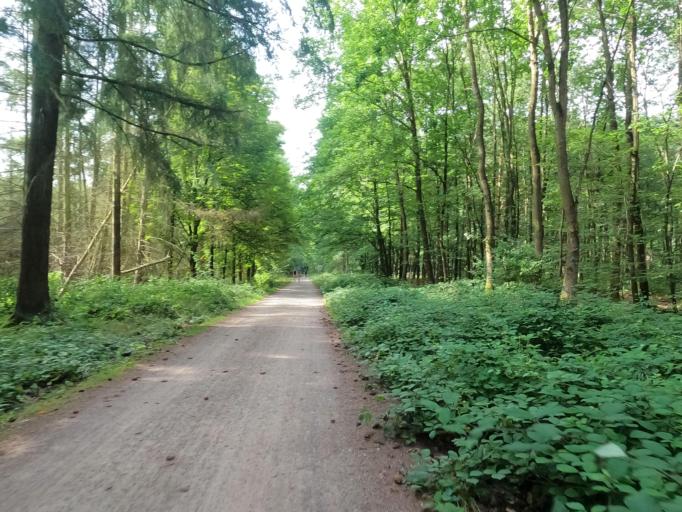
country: DE
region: Hesse
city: Langen
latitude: 50.0220
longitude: 8.6352
